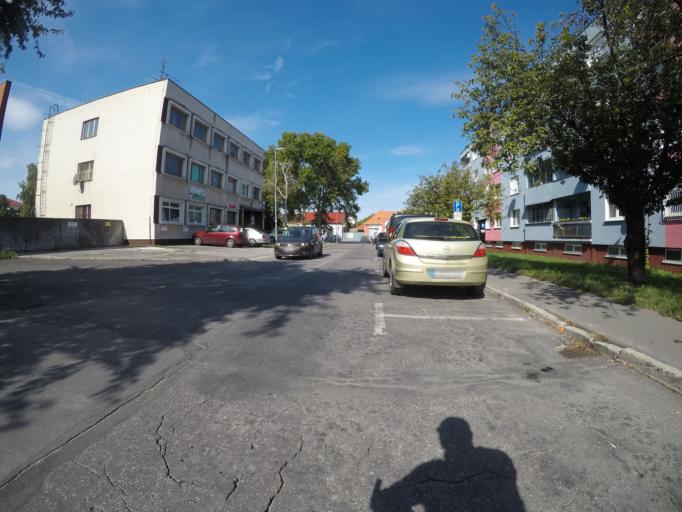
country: SK
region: Trnavsky
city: Dunajska Streda
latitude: 47.9945
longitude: 17.6207
